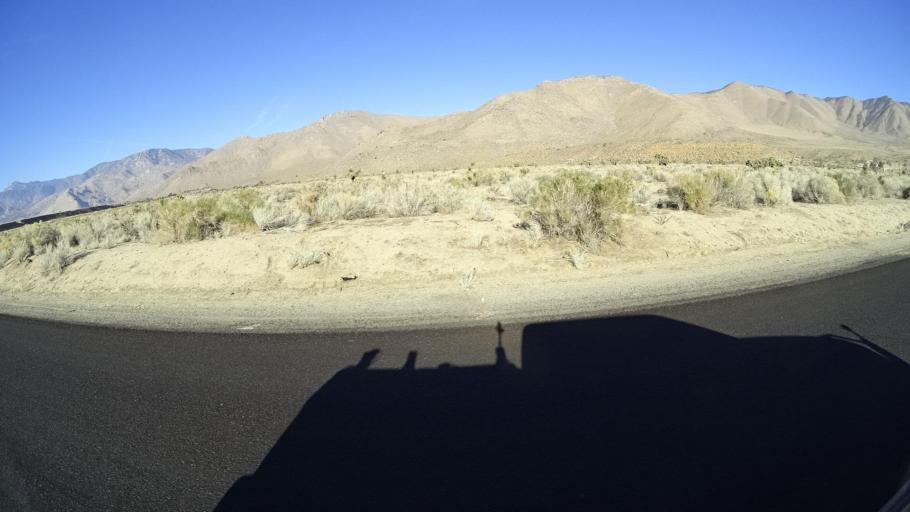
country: US
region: California
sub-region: Kern County
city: Weldon
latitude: 35.6142
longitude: -118.2478
